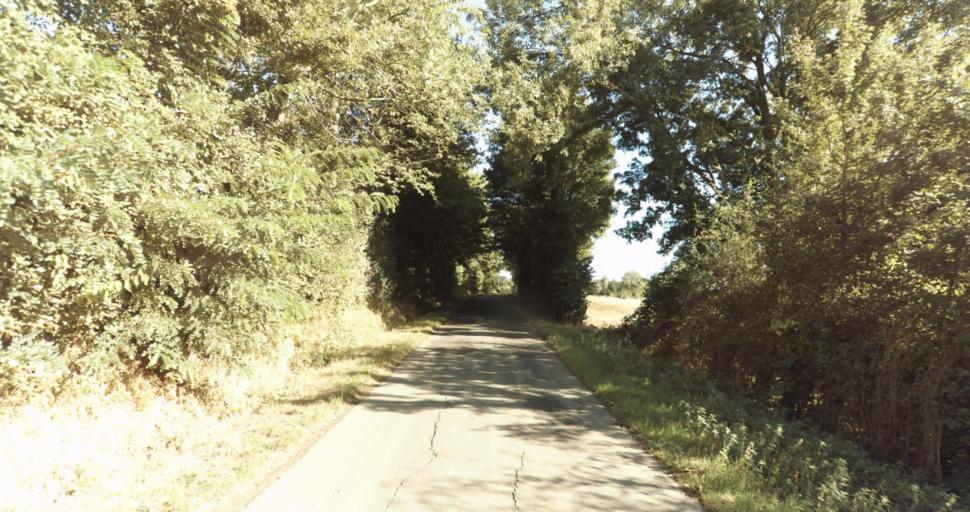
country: FR
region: Lower Normandy
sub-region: Departement de l'Orne
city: Vimoutiers
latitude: 48.9103
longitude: 0.1398
